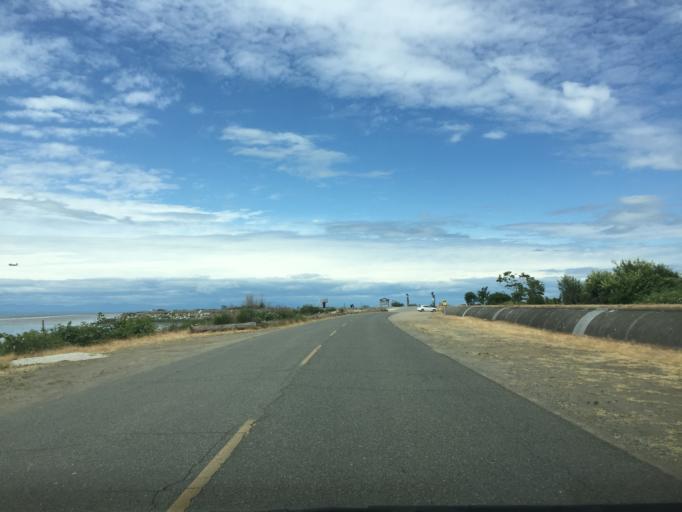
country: CA
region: British Columbia
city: Richmond
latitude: 49.2168
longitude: -123.2094
